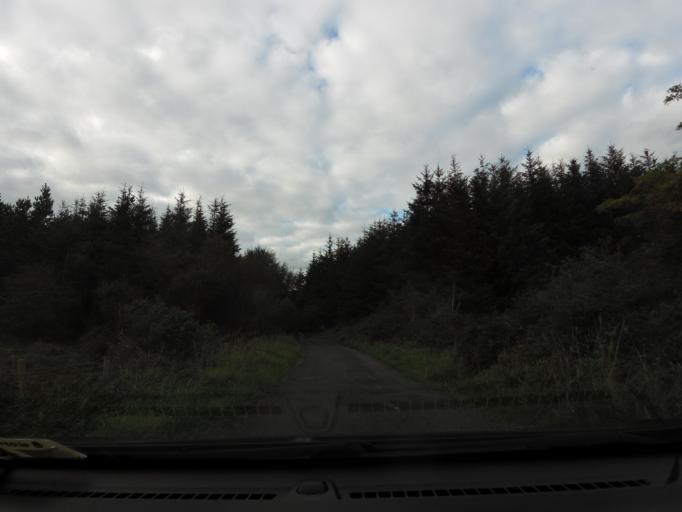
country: IE
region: Connaught
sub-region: County Galway
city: Loughrea
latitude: 53.1344
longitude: -8.5201
